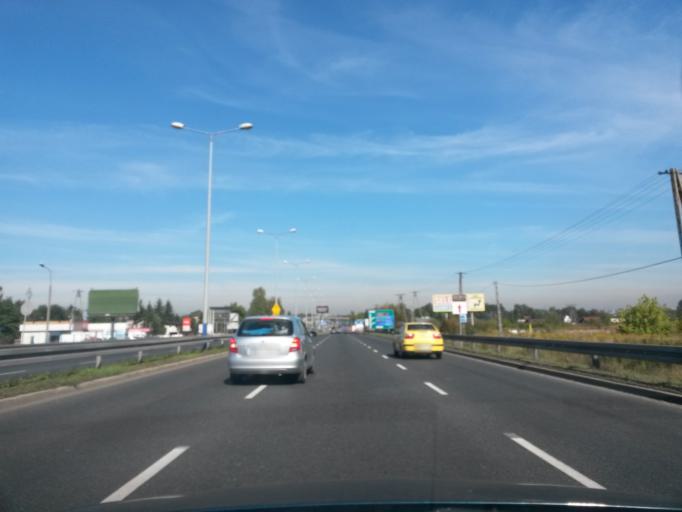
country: PL
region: Lesser Poland Voivodeship
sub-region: Powiat krakowski
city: Libertow
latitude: 49.9850
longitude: 19.9134
